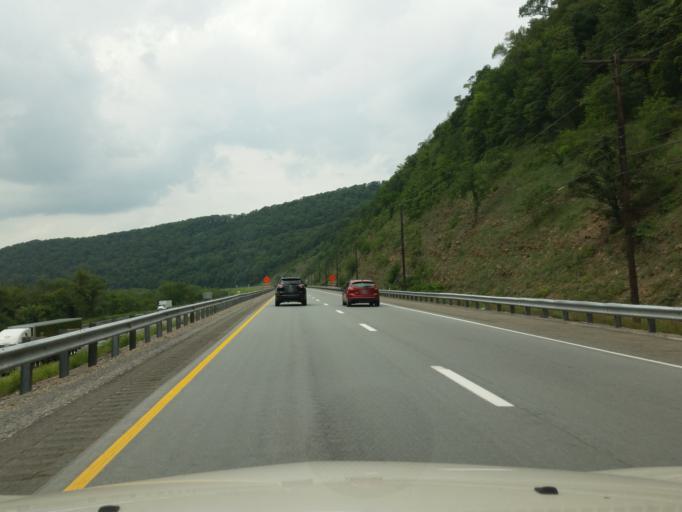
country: US
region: Pennsylvania
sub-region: Perry County
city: Newport
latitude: 40.5594
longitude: -77.1640
